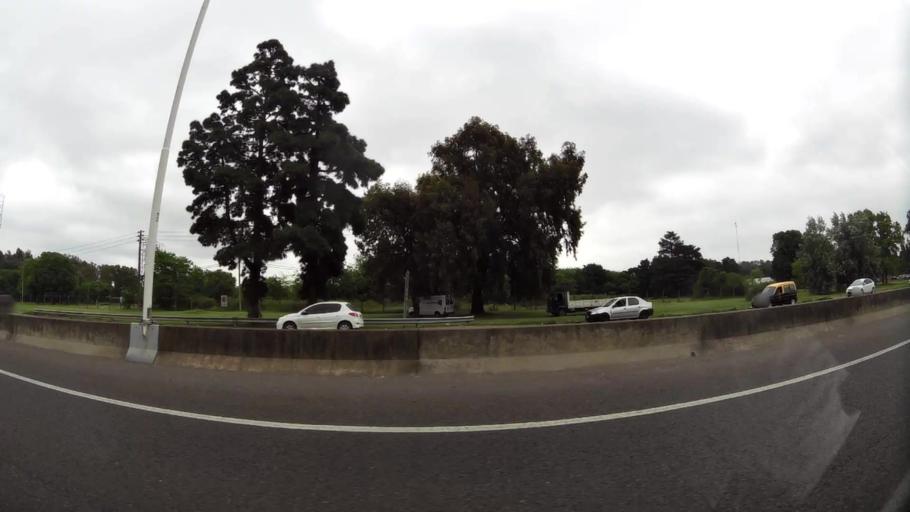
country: AR
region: Buenos Aires
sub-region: Partido de Ezeiza
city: Ezeiza
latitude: -34.7909
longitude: -58.5271
